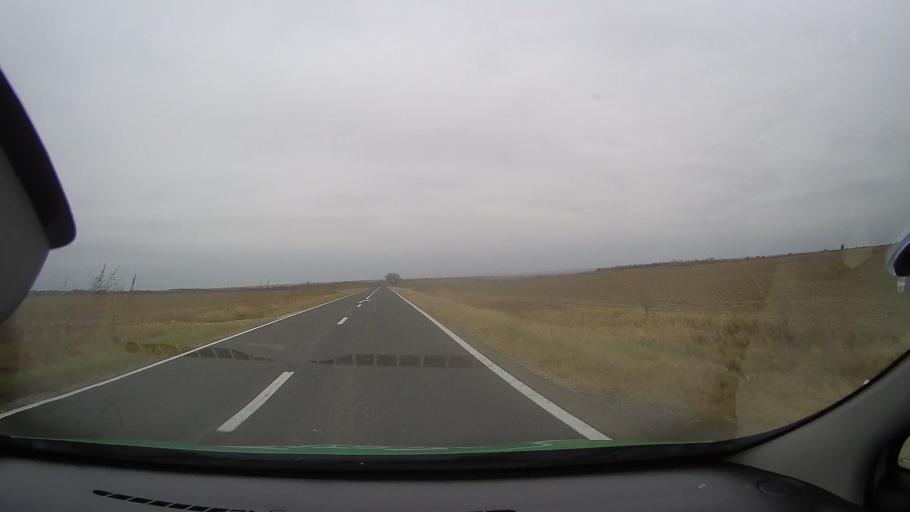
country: RO
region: Constanta
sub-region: Comuna Garliciu
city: Garliciu
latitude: 44.7107
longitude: 28.0855
